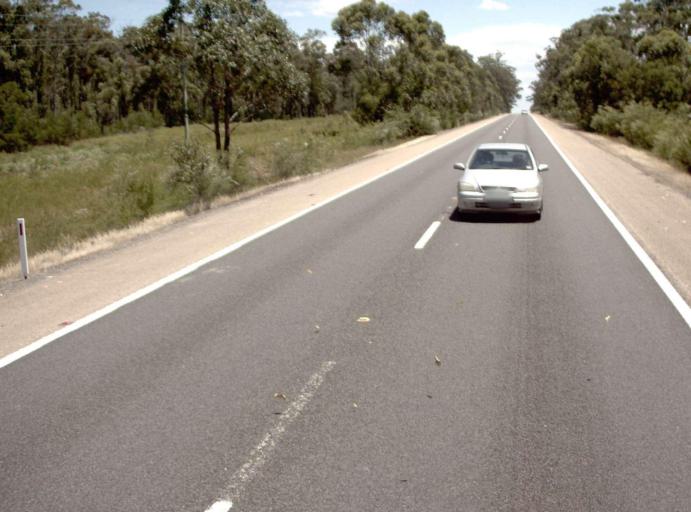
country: AU
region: Victoria
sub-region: East Gippsland
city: Lakes Entrance
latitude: -37.7534
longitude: 148.3289
